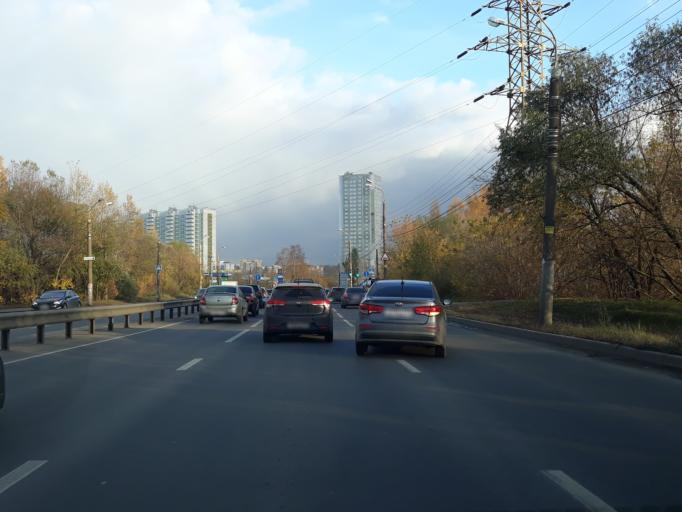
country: RU
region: Nizjnij Novgorod
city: Nizhniy Novgorod
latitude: 56.3038
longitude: 43.9148
